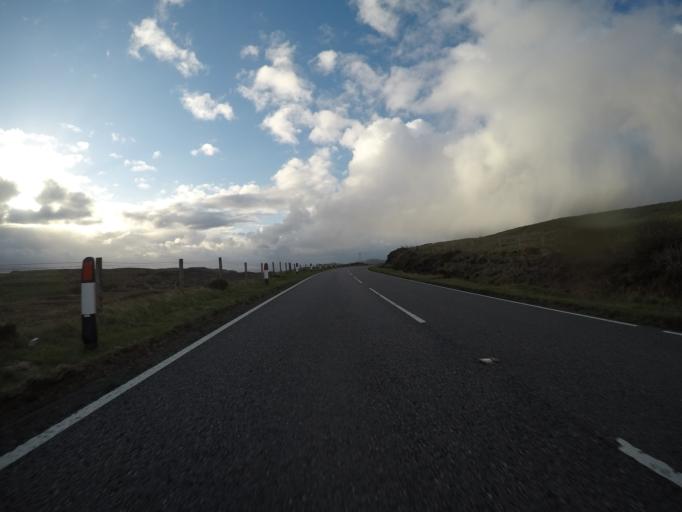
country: GB
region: Scotland
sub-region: Highland
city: Portree
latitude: 57.5516
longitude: -6.3653
